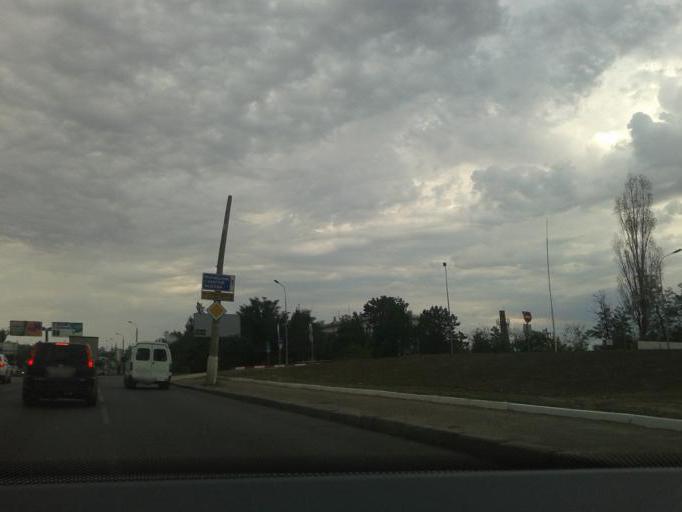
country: RU
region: Volgograd
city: Volgograd
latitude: 48.6468
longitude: 44.4339
